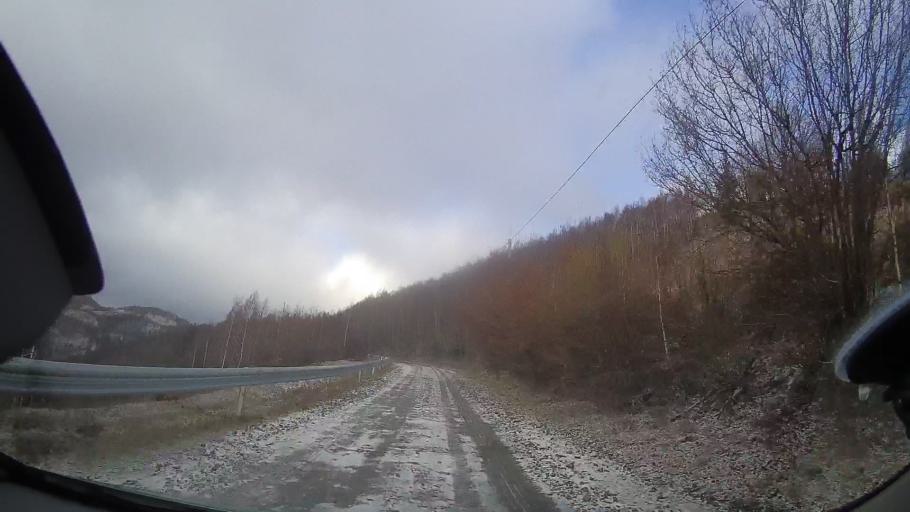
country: RO
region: Cluj
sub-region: Comuna Valea Ierii
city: Valea Ierii
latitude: 46.6500
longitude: 23.3556
